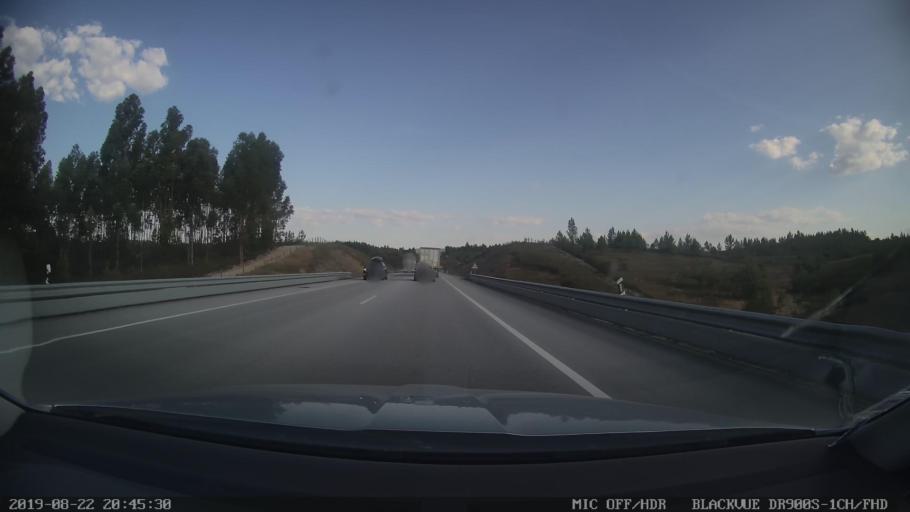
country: PT
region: Castelo Branco
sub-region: Proenca-A-Nova
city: Proenca-a-Nova
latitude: 39.7162
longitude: -7.8660
